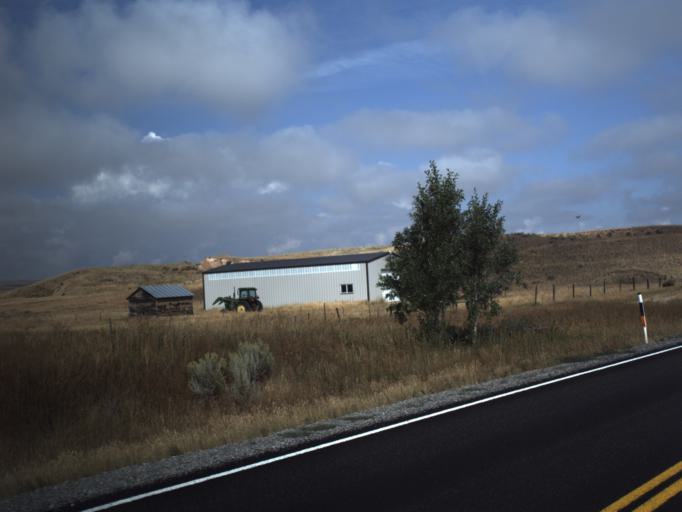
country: US
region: Utah
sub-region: Rich County
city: Randolph
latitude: 41.5355
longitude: -111.1628
